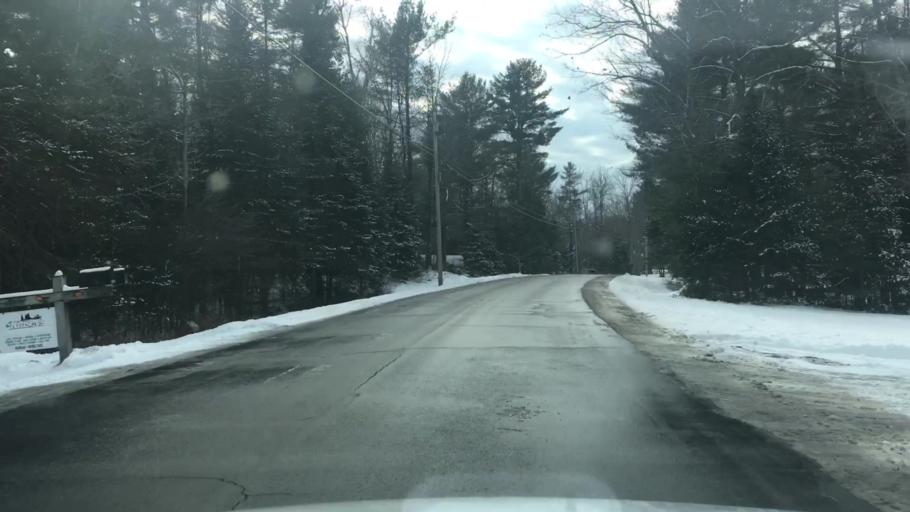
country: US
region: Maine
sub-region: Kennebec County
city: Chelsea
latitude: 44.2804
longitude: -69.6702
